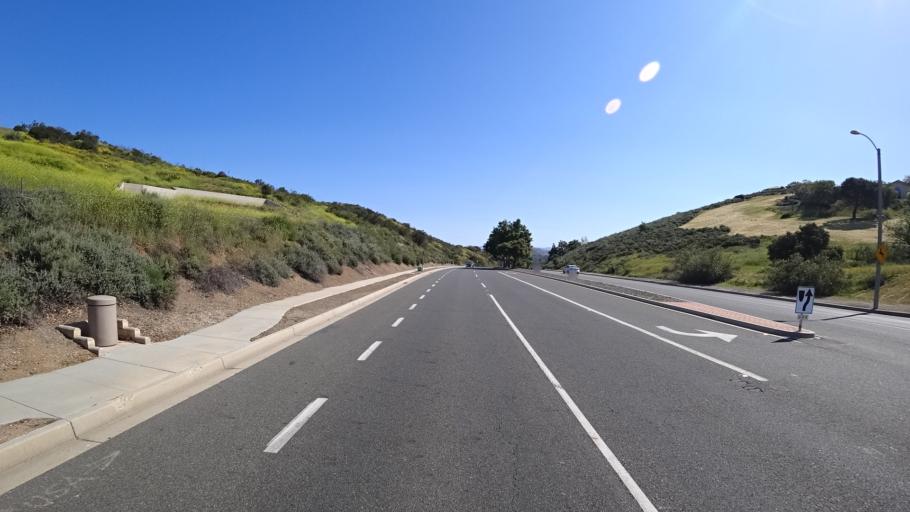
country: US
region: California
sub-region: Ventura County
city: Casa Conejo
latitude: 34.1731
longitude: -118.9321
